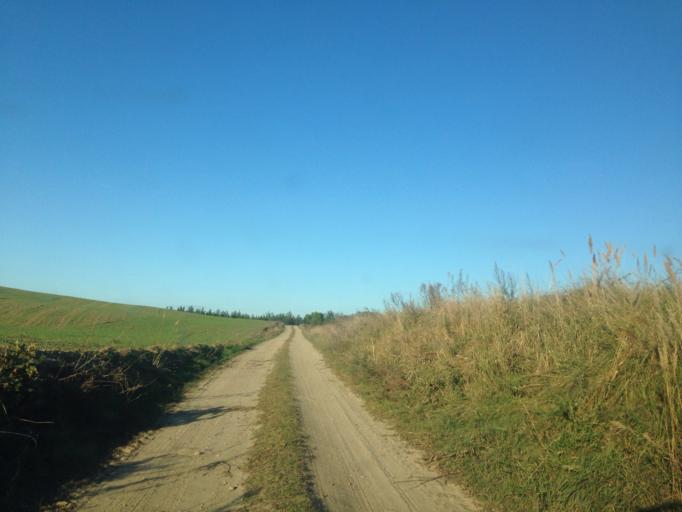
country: PL
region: Kujawsko-Pomorskie
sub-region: Powiat brodnicki
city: Bartniczka
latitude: 53.2767
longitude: 19.6814
